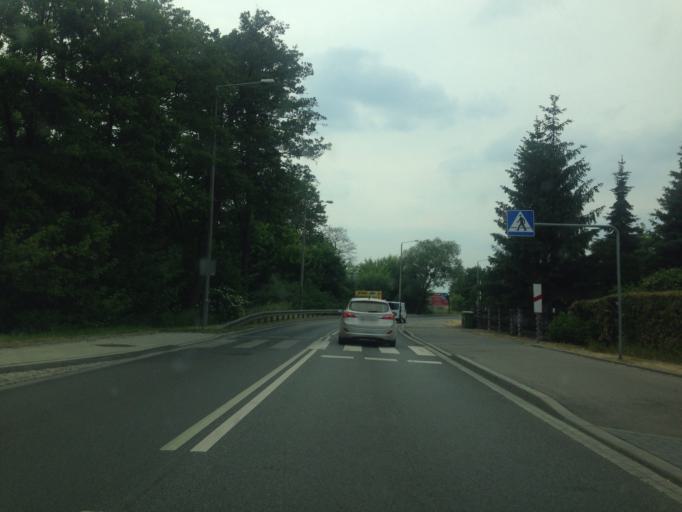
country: PL
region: Kujawsko-Pomorskie
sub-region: Powiat grudziadzki
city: Rogozno
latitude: 53.5020
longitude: 18.8477
